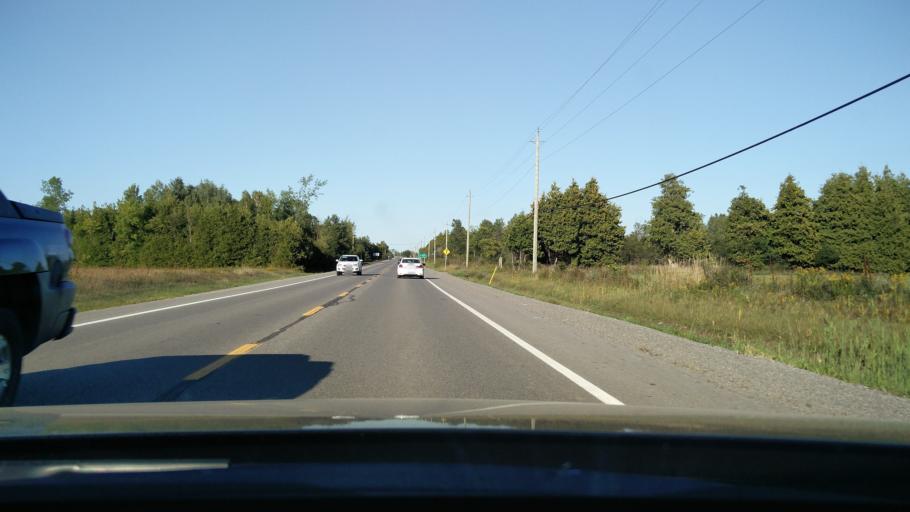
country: CA
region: Ontario
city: Carleton Place
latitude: 45.1302
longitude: -75.9408
